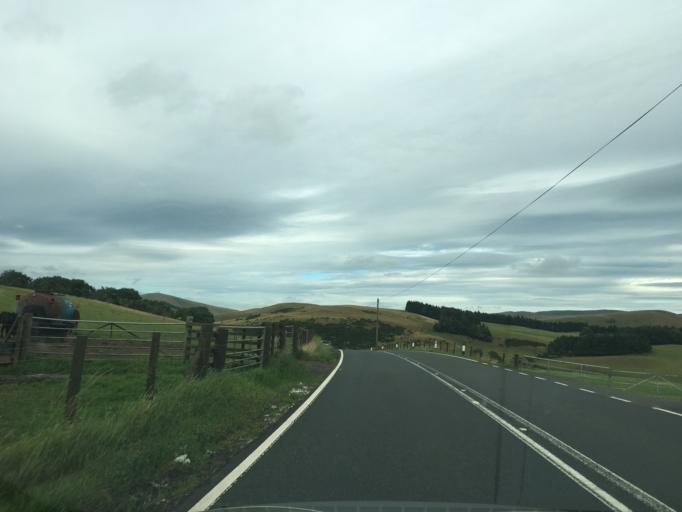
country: GB
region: Scotland
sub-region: South Lanarkshire
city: Biggar
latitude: 55.6436
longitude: -3.4914
